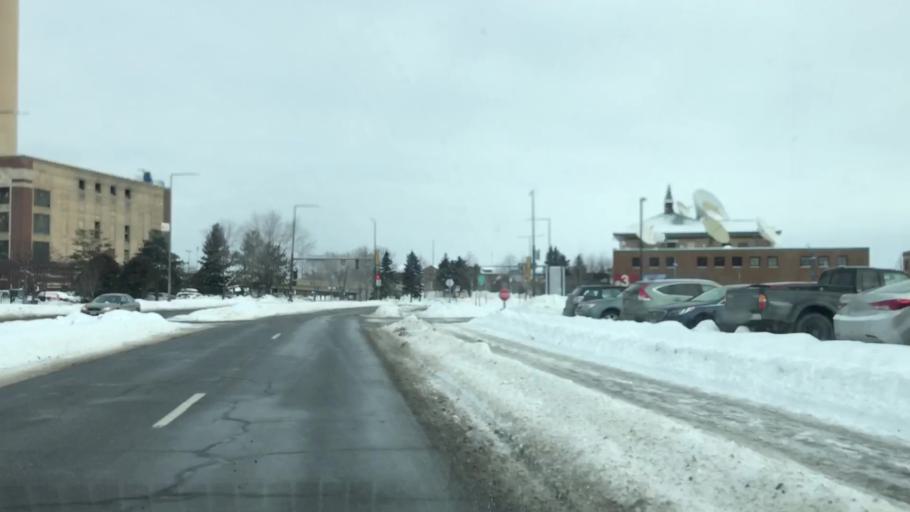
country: US
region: Minnesota
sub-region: Saint Louis County
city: Duluth
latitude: 46.7840
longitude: -92.0979
